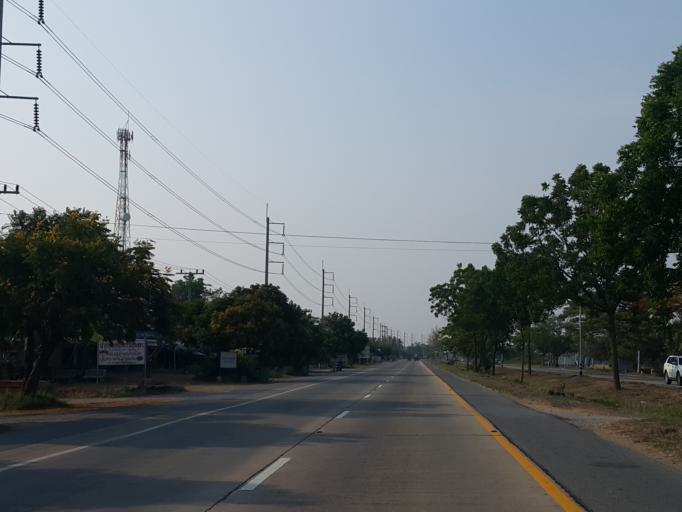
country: TH
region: Chai Nat
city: Hankha
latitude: 14.9352
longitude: 100.0827
